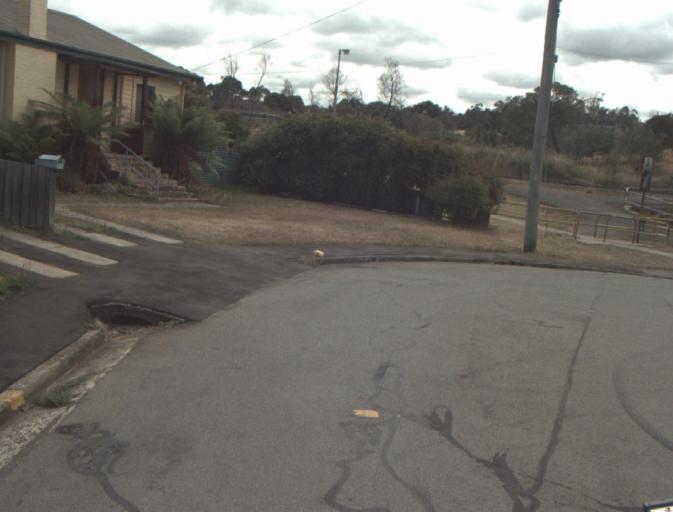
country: AU
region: Tasmania
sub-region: Launceston
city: Mayfield
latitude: -41.3821
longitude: 147.1313
